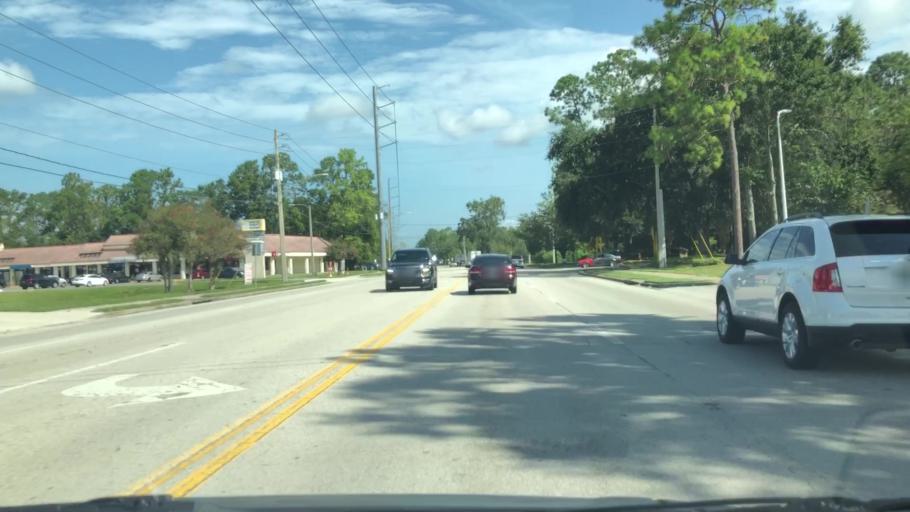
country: US
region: Florida
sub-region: Saint Johns County
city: Fruit Cove
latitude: 30.1743
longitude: -81.6038
